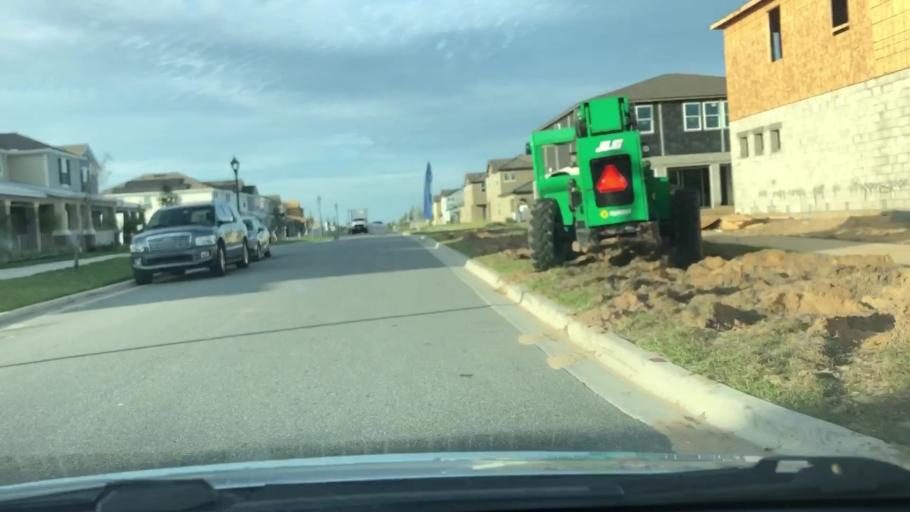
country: US
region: Florida
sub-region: Polk County
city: Citrus Ridge
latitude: 28.4318
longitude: -81.6236
